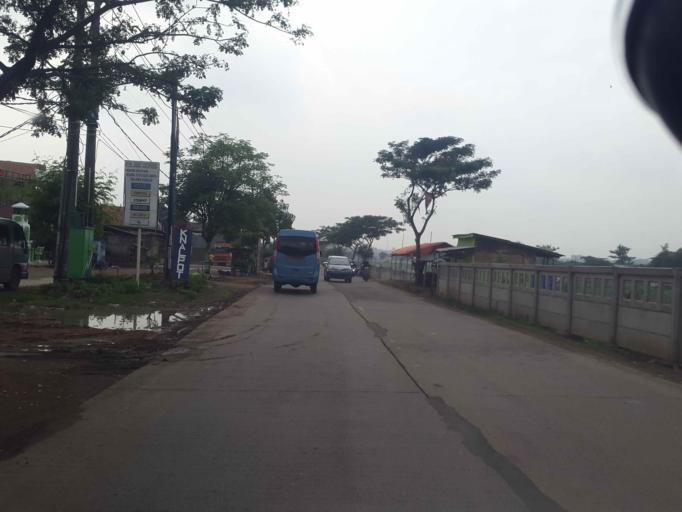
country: ID
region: West Java
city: Cikarang
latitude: -6.3133
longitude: 107.1529
